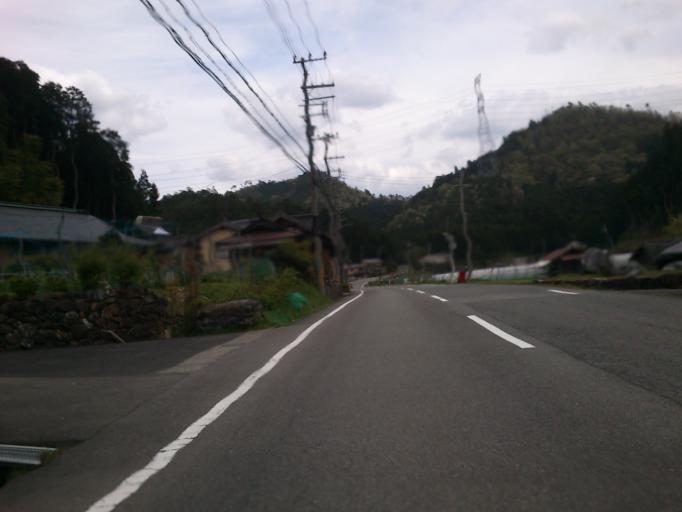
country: JP
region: Kyoto
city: Kameoka
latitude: 35.2056
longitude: 135.6123
